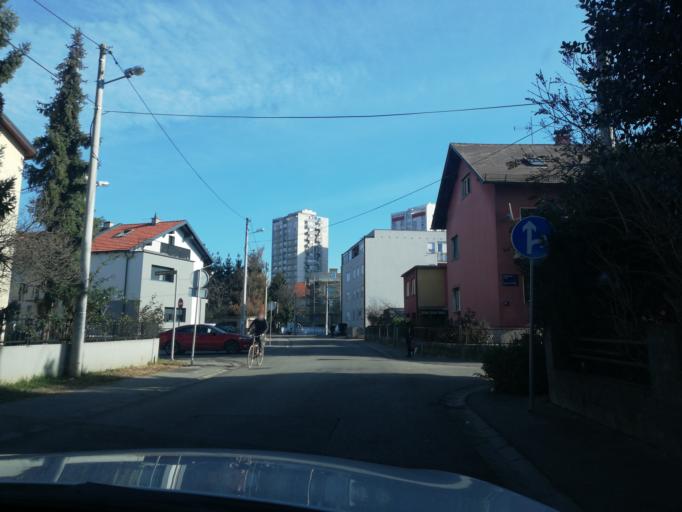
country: HR
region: Grad Zagreb
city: Zagreb - Centar
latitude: 45.8004
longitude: 15.9481
